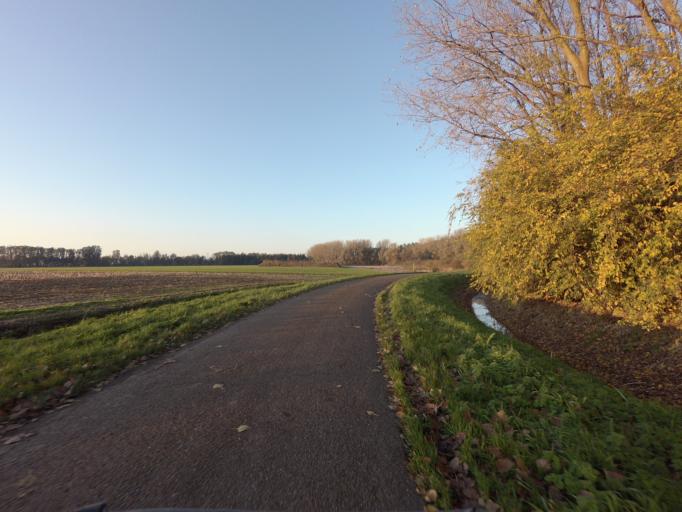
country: NL
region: North Brabant
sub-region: Gemeente Woudrichem
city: Woudrichem
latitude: 51.7914
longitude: 5.0205
